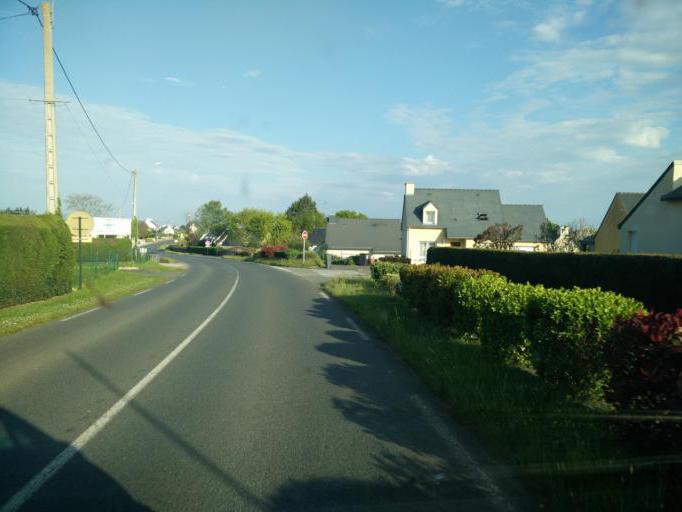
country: FR
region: Brittany
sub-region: Departement des Cotes-d'Armor
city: Erquy
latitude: 48.6263
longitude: -2.4497
